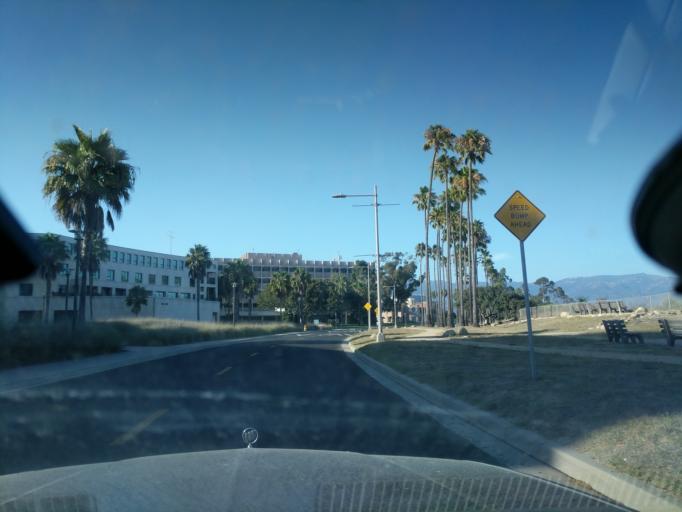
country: US
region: California
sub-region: Santa Barbara County
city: Isla Vista
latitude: 34.4122
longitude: -119.8418
